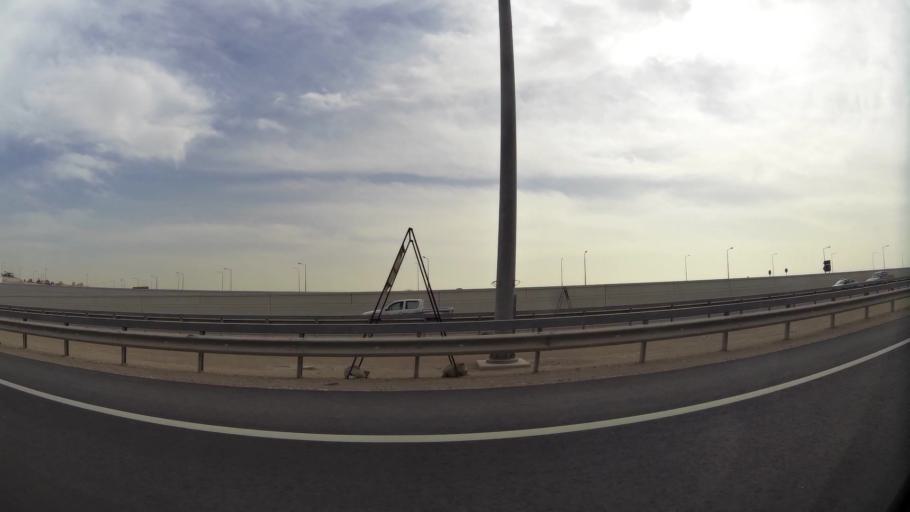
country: QA
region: Baladiyat ar Rayyan
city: Ar Rayyan
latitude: 25.3225
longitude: 51.3491
